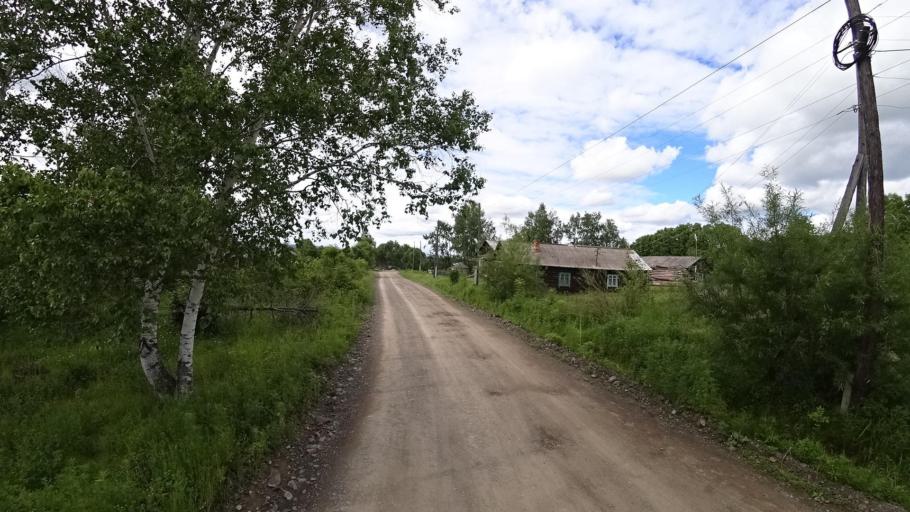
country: RU
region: Khabarovsk Krai
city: Litovko
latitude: 49.3657
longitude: 135.1736
